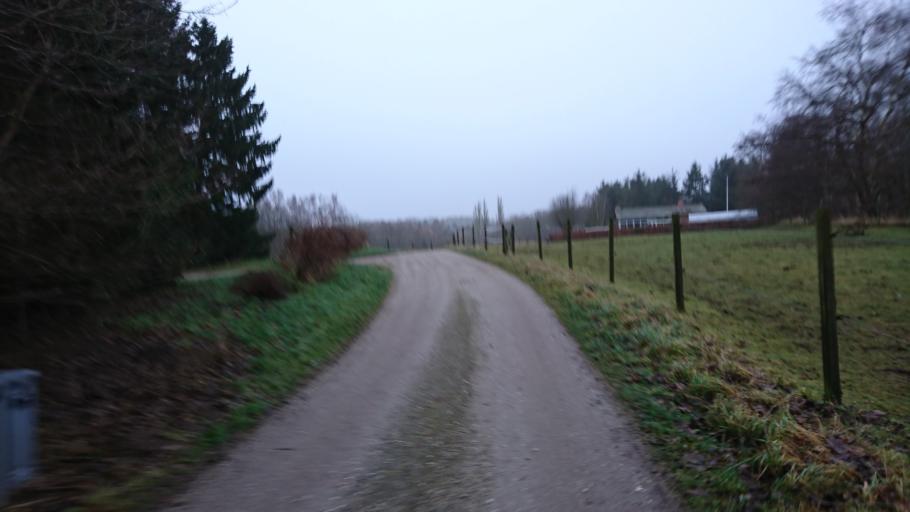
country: DK
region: Capital Region
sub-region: Ballerup Kommune
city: Ballerup
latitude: 55.7458
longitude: 12.3476
